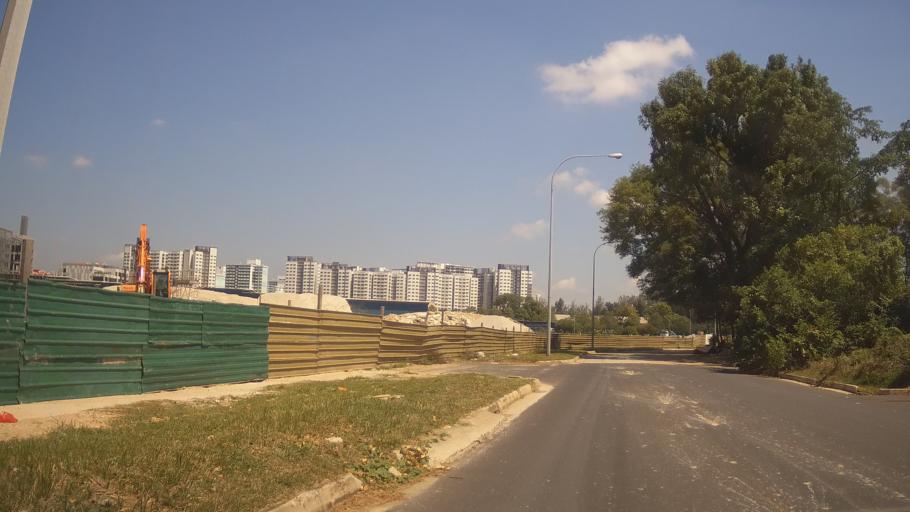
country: SG
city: Singapore
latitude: 1.3217
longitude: 103.7250
